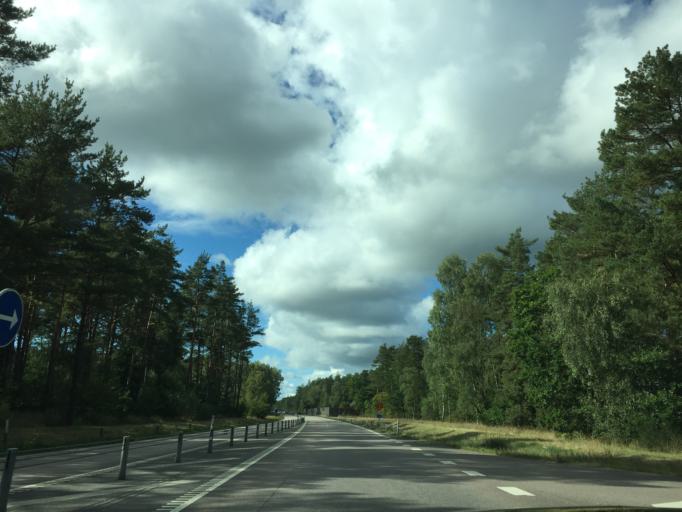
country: SE
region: Skane
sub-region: Sjobo Kommun
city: Sjoebo
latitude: 55.6361
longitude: 13.6686
